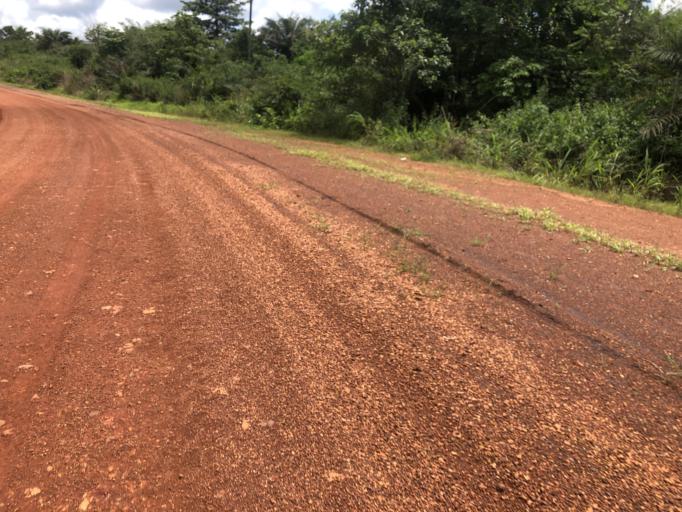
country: SL
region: Northern Province
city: Port Loko
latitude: 8.7181
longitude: -12.8371
